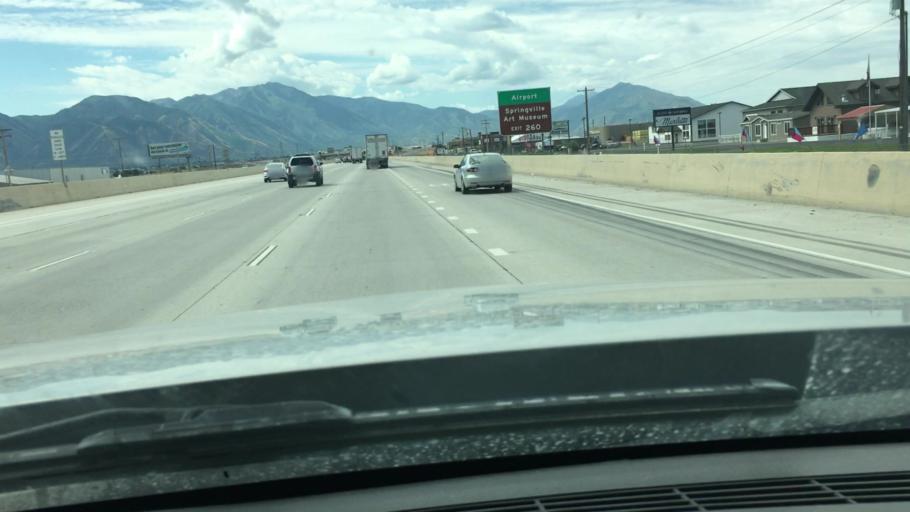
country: US
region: Utah
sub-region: Utah County
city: Springville
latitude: 40.1696
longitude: -111.6473
